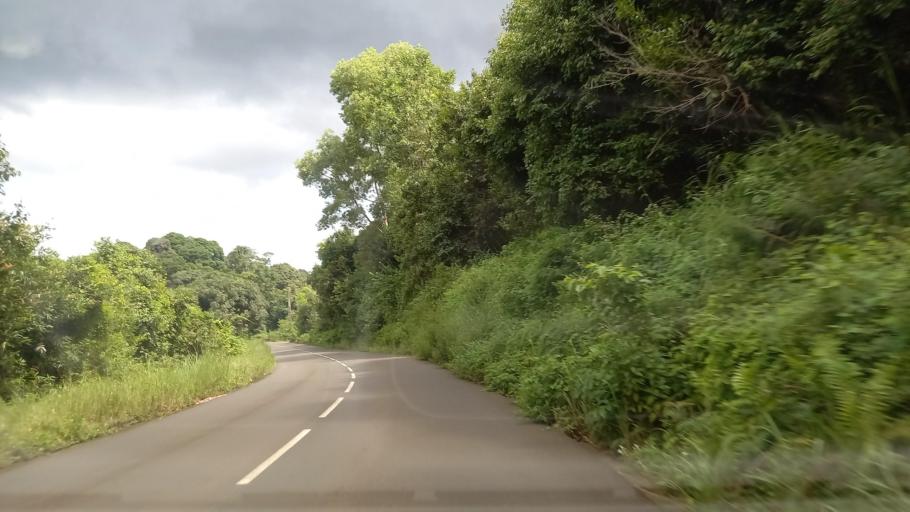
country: YT
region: Tsingoni
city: Tsingoni
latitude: -12.7884
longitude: 45.1612
